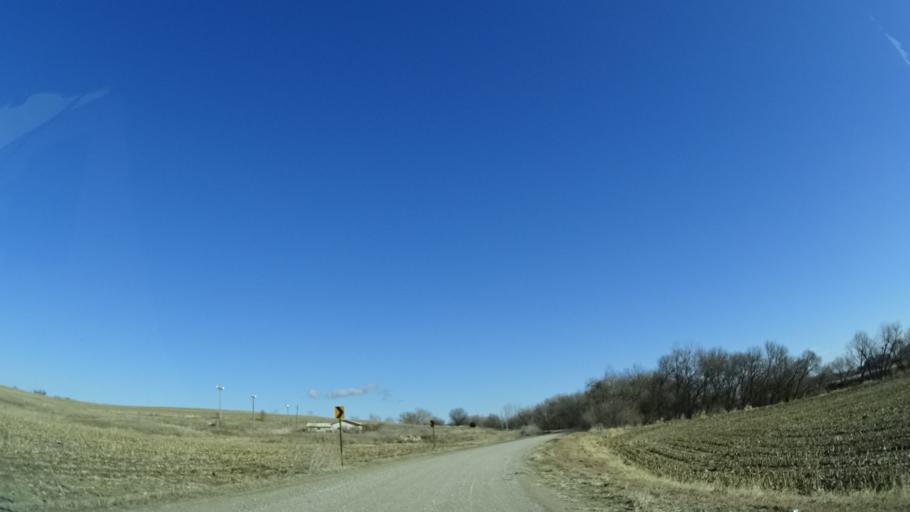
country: US
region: Nebraska
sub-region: Sarpy County
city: Offutt Air Force Base
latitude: 41.1471
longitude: -95.9581
